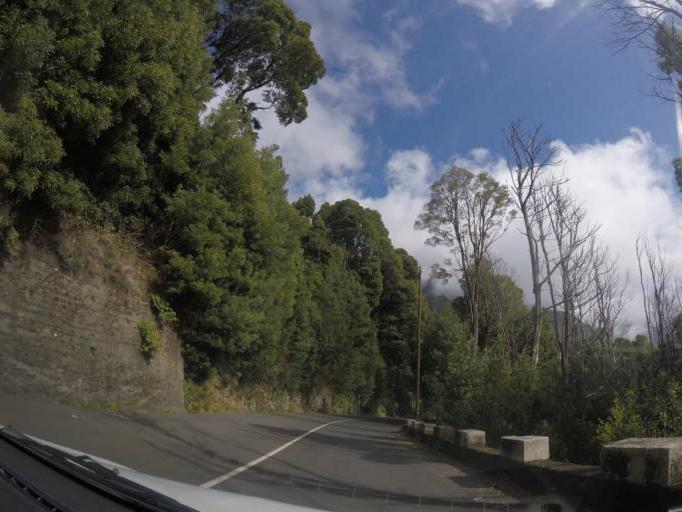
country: PT
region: Madeira
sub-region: Sao Vicente
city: Sao Vicente
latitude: 32.7539
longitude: -17.0223
